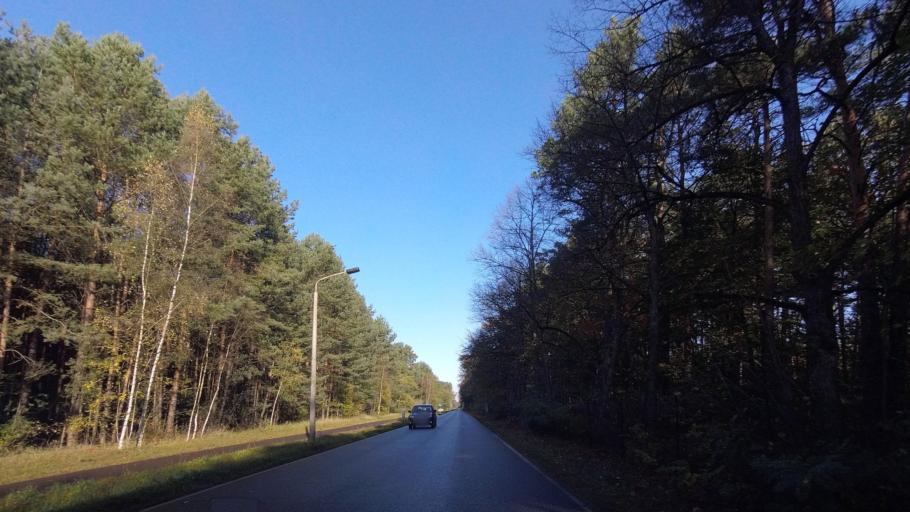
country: DE
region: Brandenburg
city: Borkheide
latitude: 52.2323
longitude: 12.8549
